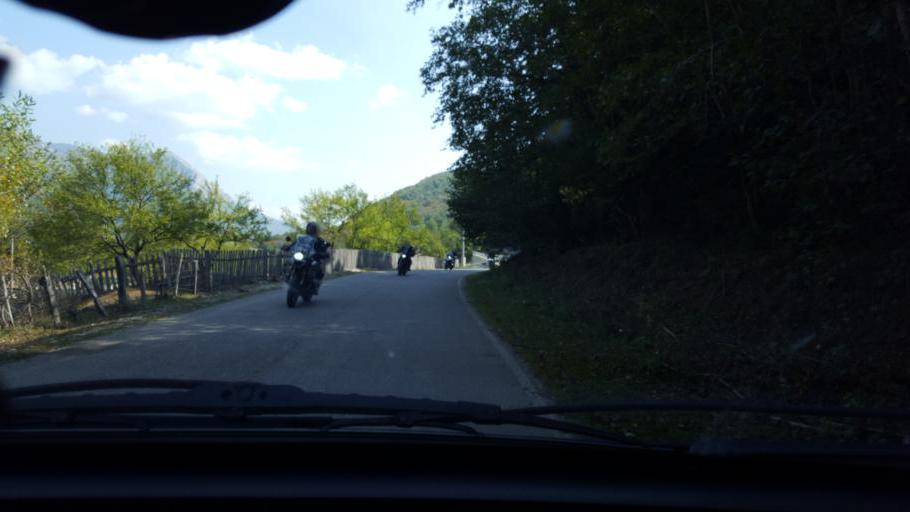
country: ME
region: Andrijevica
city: Andrijevica
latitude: 42.5806
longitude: 19.7376
